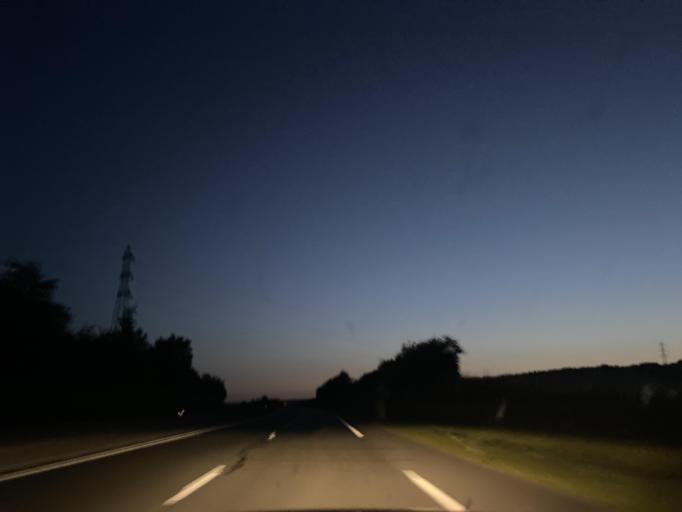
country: FR
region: Haute-Normandie
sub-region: Departement de l'Eure
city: Gravigny
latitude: 49.0393
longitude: 1.1858
